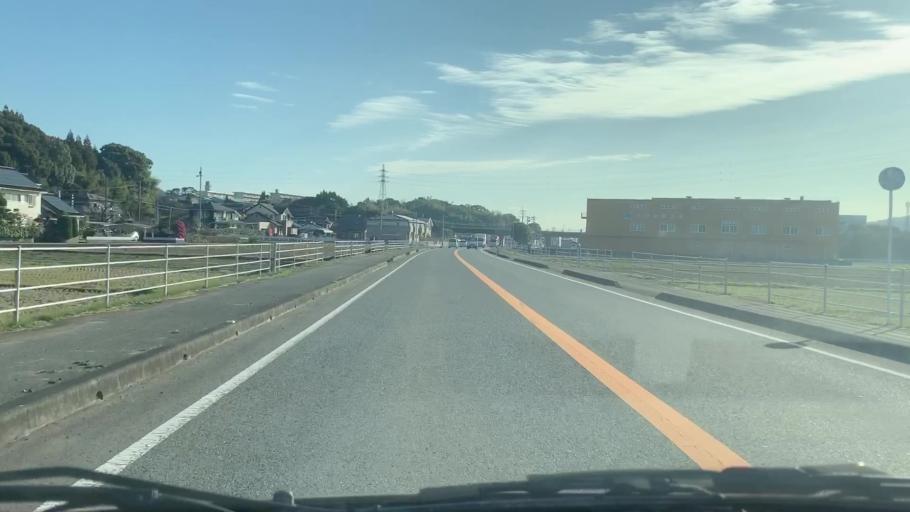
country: JP
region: Saga Prefecture
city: Takeocho-takeo
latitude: 33.2239
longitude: 130.0464
